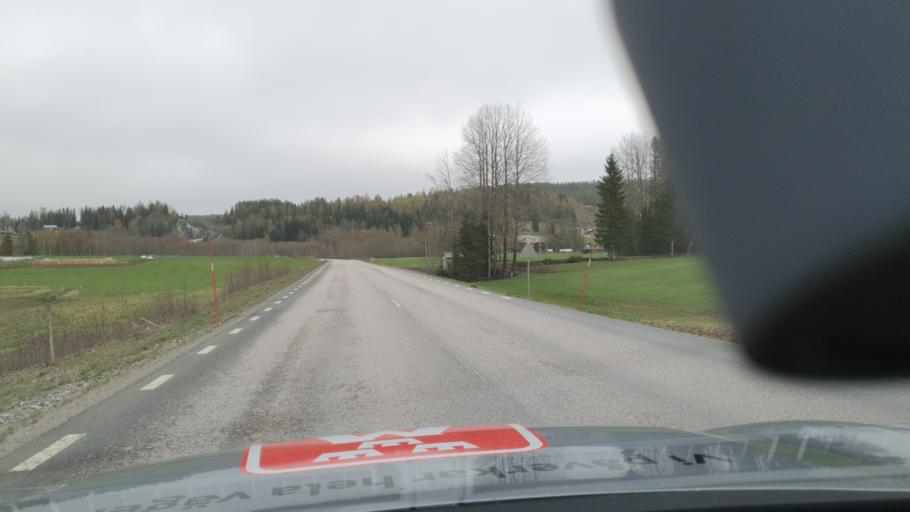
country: SE
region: Vaesternorrland
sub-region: OErnskoeldsviks Kommun
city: Ornskoldsvik
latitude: 63.3377
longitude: 18.7982
